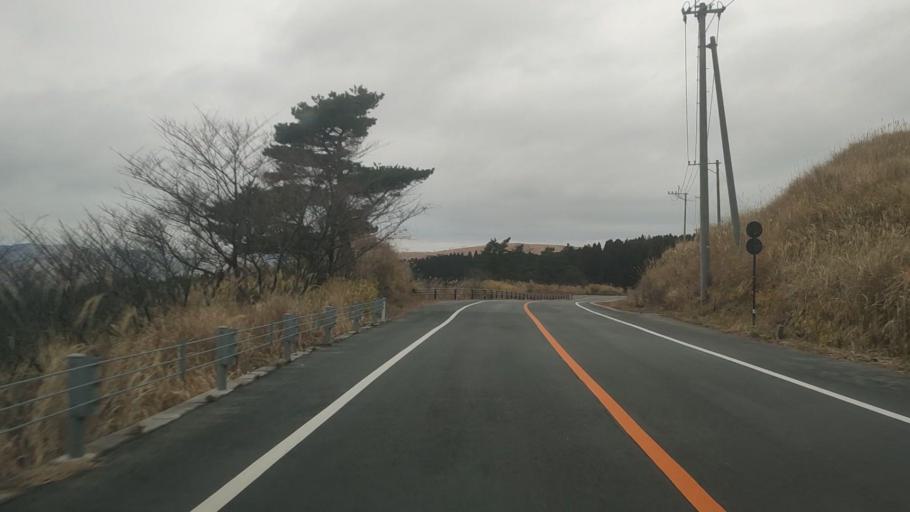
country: JP
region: Kumamoto
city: Aso
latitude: 32.8945
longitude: 131.0271
